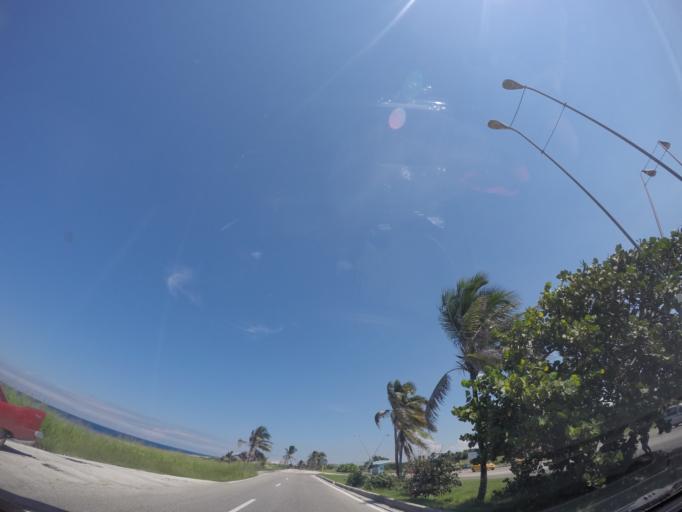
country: CU
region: La Habana
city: Centro Habana
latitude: 23.1535
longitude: -82.3513
